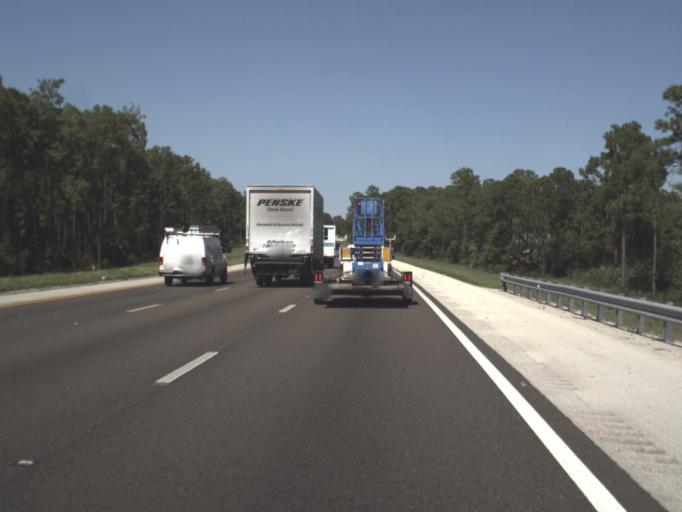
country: US
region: Florida
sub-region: Collier County
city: Vineyards
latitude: 26.2467
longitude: -81.7370
